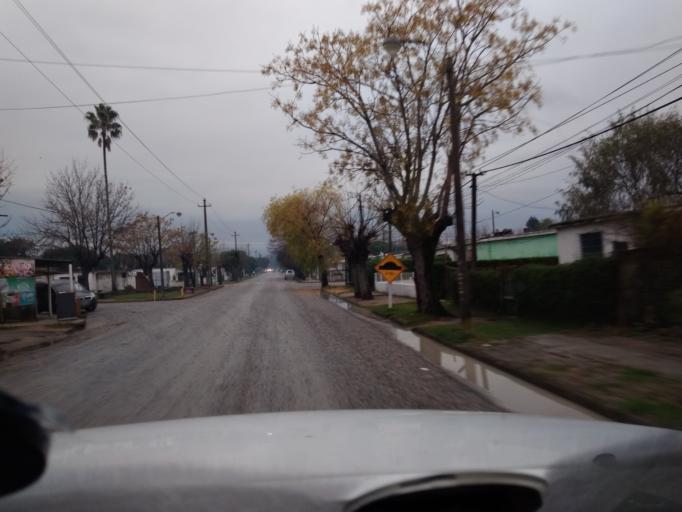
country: UY
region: Florida
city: Florida
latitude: -34.1076
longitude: -56.2127
